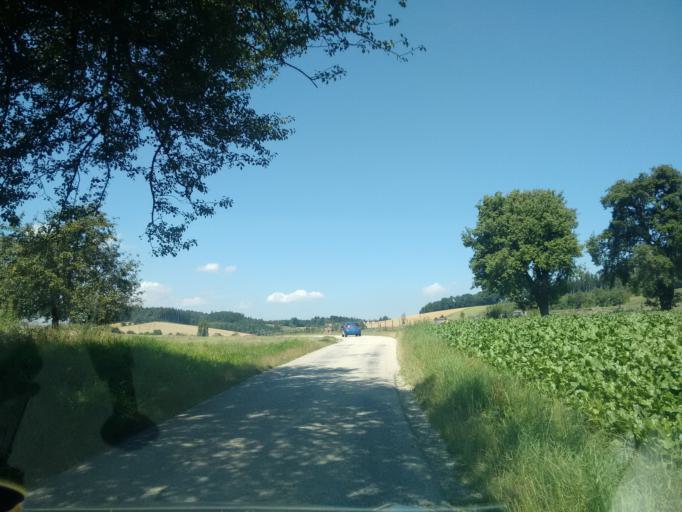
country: AT
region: Upper Austria
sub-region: Wels-Land
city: Gunskirchen
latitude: 48.1764
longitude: 13.9575
